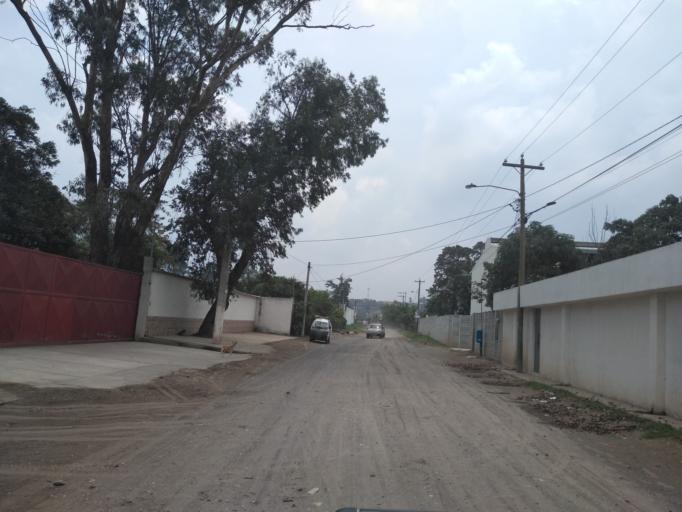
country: GT
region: Guatemala
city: Petapa
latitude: 14.5036
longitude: -90.5489
